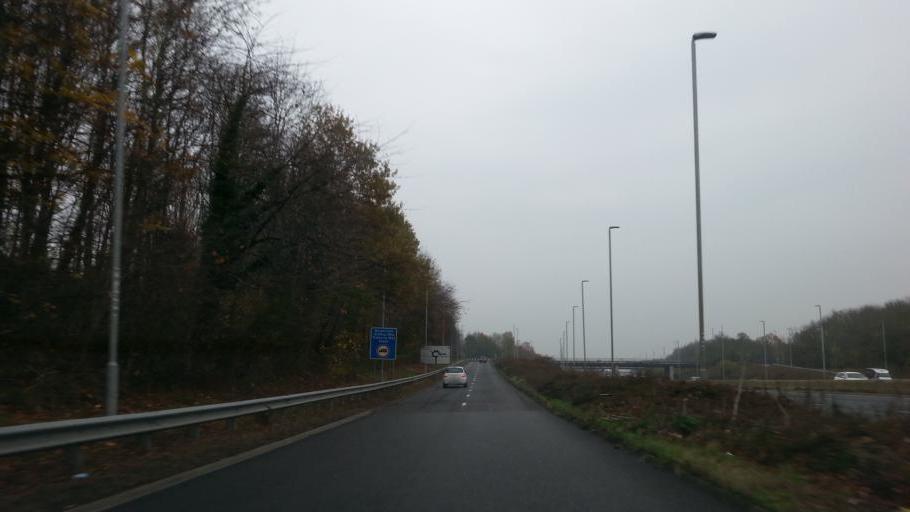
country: GB
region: England
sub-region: Cambridgeshire
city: Yaxley
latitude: 52.5406
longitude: -0.2869
